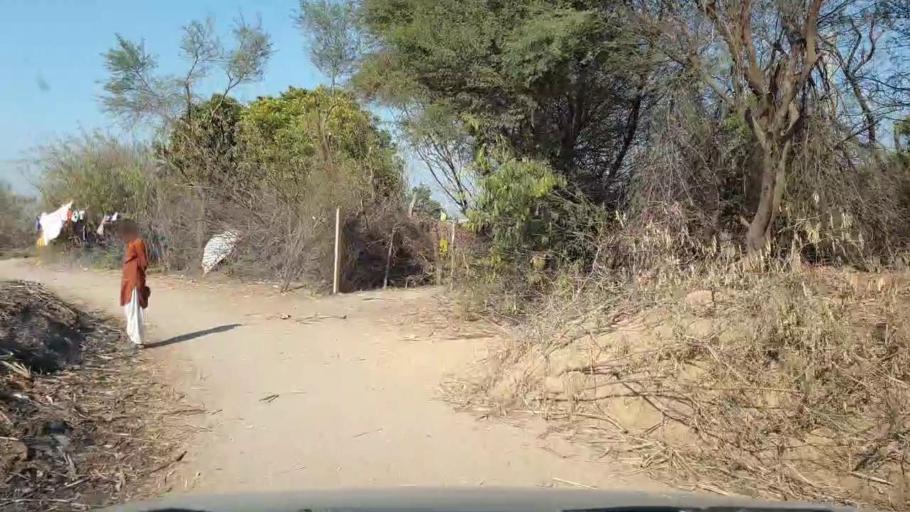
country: PK
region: Sindh
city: Tando Jam
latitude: 25.4373
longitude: 68.6158
